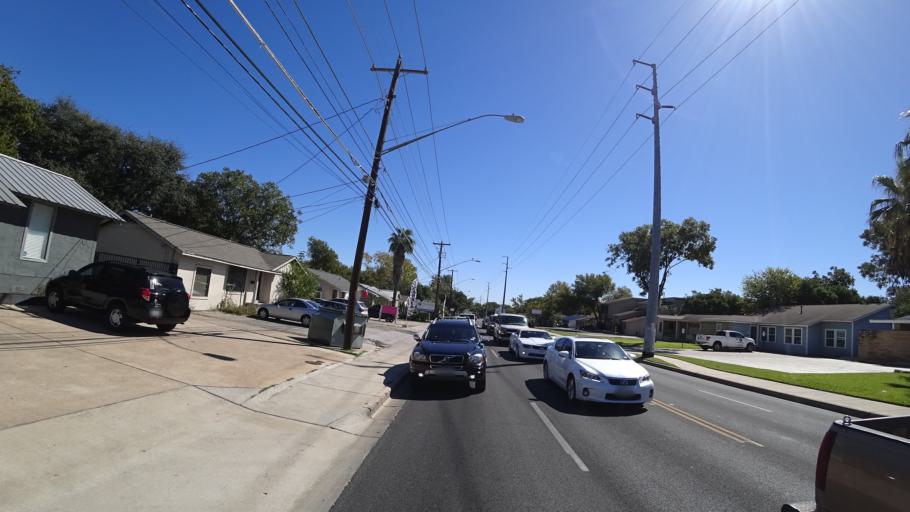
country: US
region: Texas
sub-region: Travis County
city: Austin
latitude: 30.3342
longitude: -97.7384
